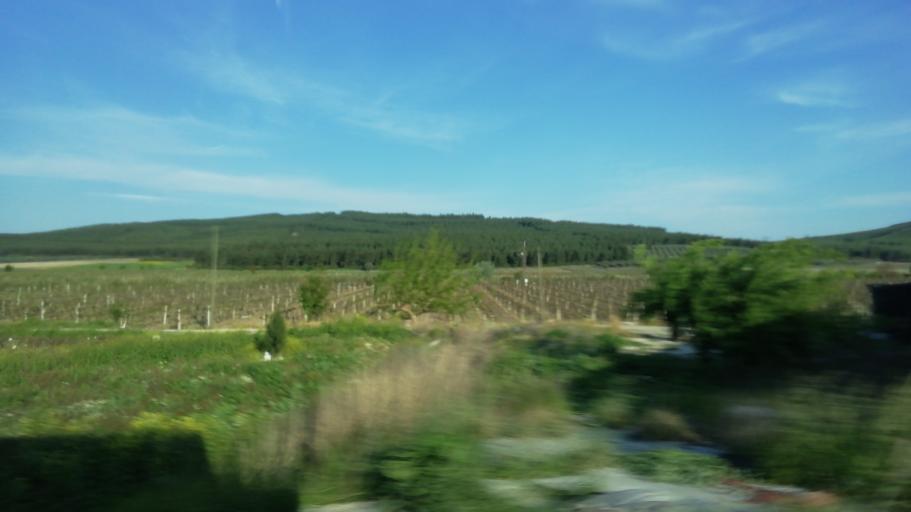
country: TR
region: Manisa
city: Halitpasa
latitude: 38.7996
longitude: 27.6880
